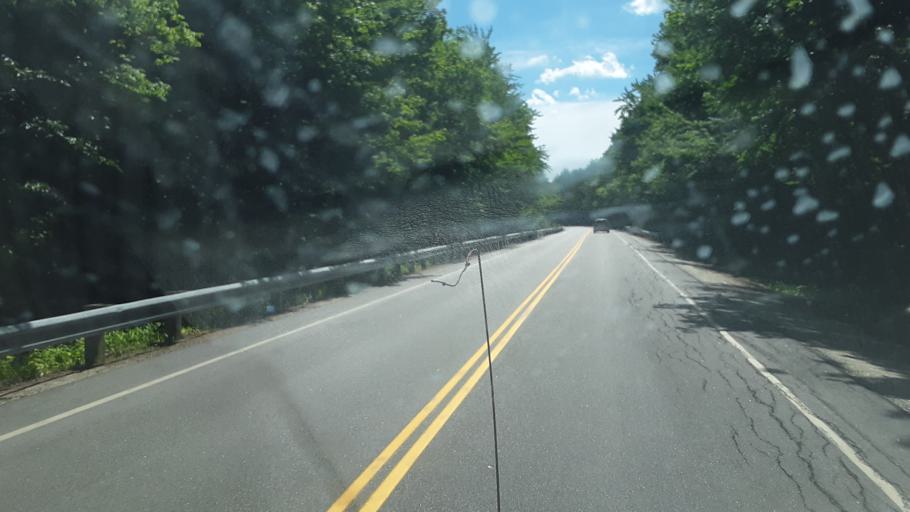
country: US
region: New Hampshire
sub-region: Carroll County
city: Tamworth
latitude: 43.9988
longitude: -71.3987
